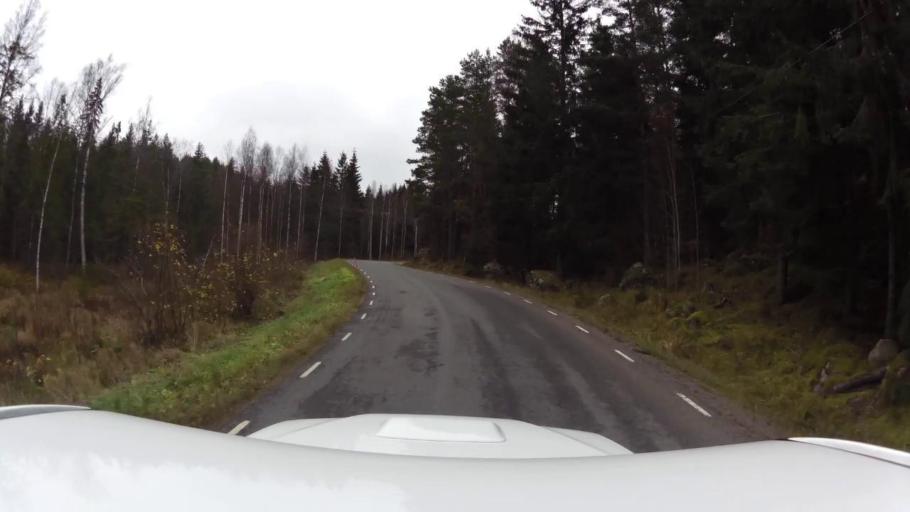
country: SE
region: OEstergoetland
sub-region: Kinda Kommun
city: Rimforsa
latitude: 58.1360
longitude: 15.5884
